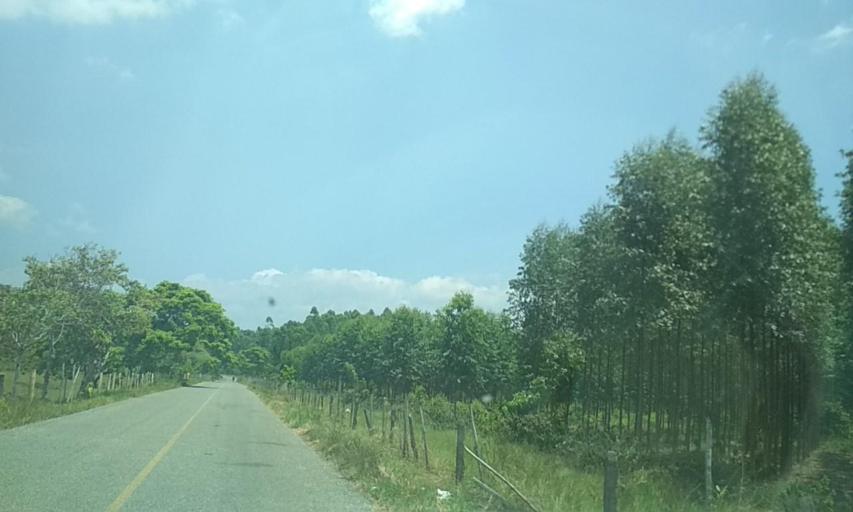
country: MX
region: Tabasco
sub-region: Huimanguillo
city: Francisco Rueda
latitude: 17.8383
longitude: -93.9081
